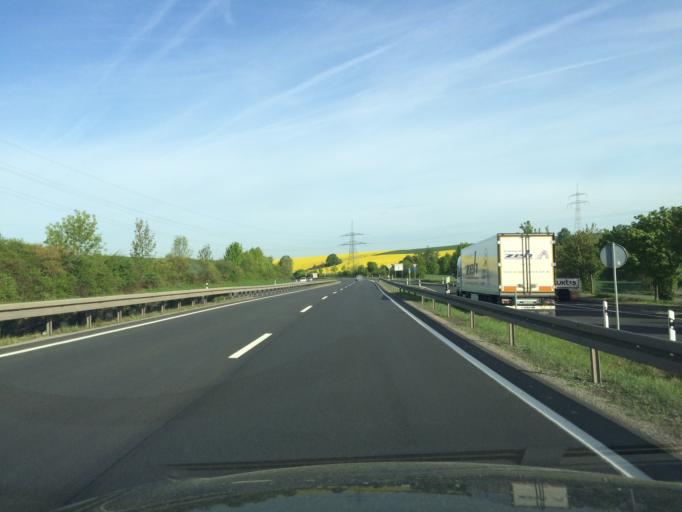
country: DE
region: Bavaria
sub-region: Regierungsbezirk Unterfranken
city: Rottendorf
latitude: 49.7785
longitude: 10.0525
